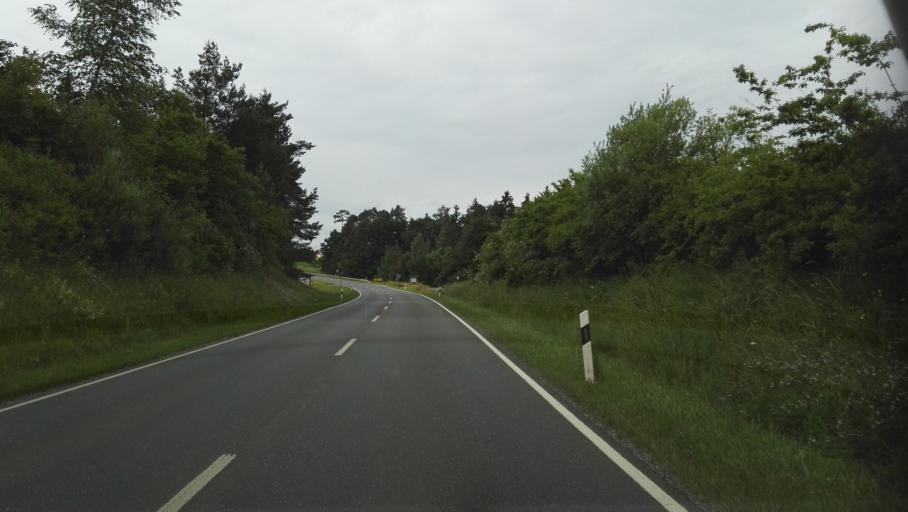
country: DE
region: Bavaria
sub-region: Upper Franconia
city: Hollfeld
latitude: 49.9248
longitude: 11.3047
